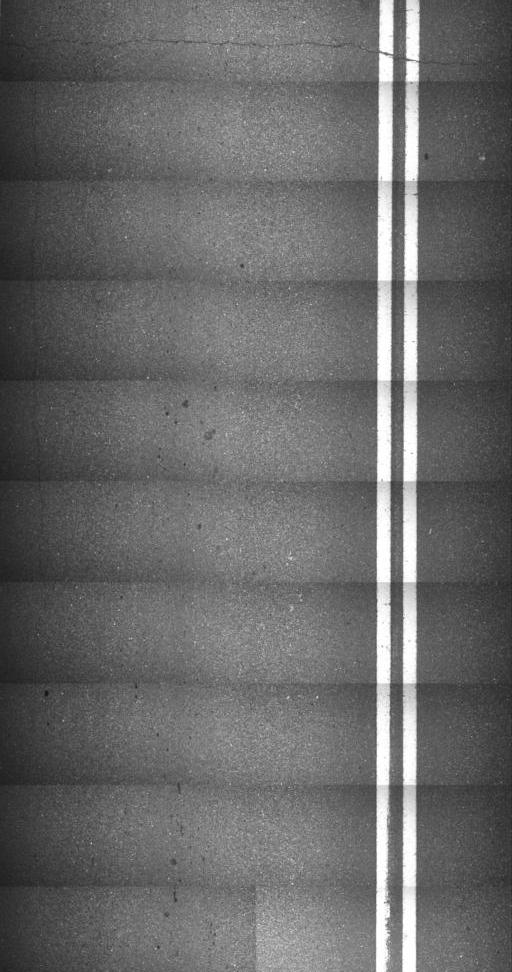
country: US
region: Vermont
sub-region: Windham County
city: Bellows Falls
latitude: 43.0999
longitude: -72.4434
